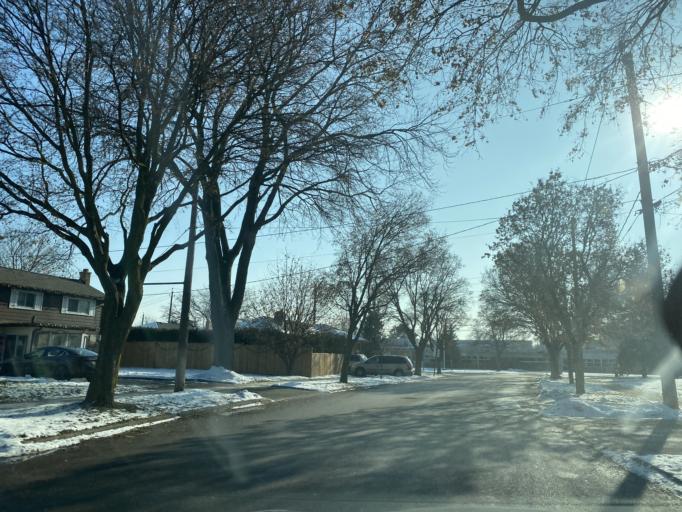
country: CA
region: Ontario
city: Etobicoke
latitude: 43.6607
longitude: -79.5661
